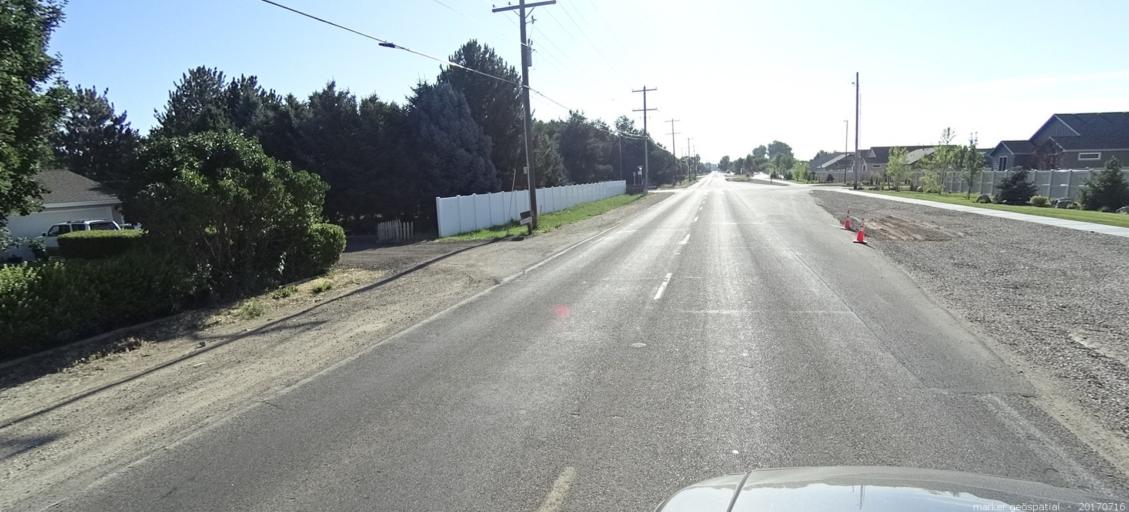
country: US
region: Idaho
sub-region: Ada County
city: Meridian
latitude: 43.5465
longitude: -116.3119
